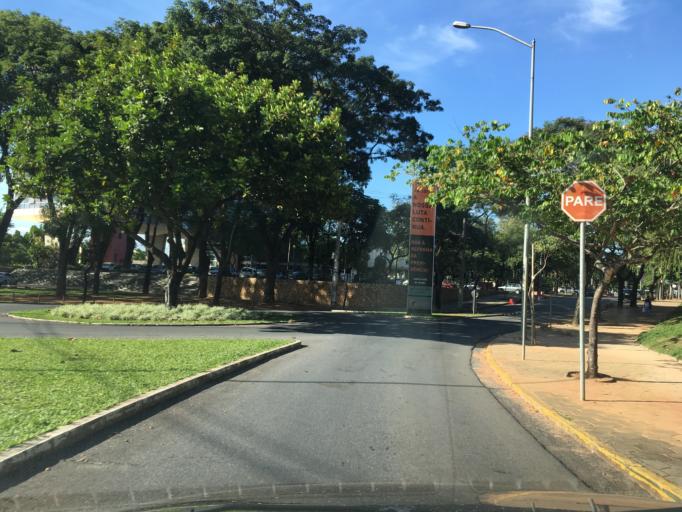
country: BR
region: Minas Gerais
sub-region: Belo Horizonte
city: Belo Horizonte
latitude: -19.8649
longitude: -43.9643
